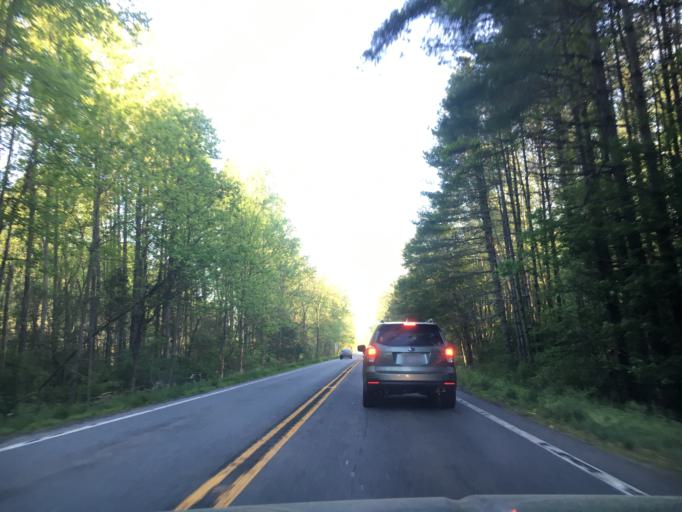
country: US
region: Virginia
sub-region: Campbell County
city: Rustburg
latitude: 37.2951
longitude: -79.1096
